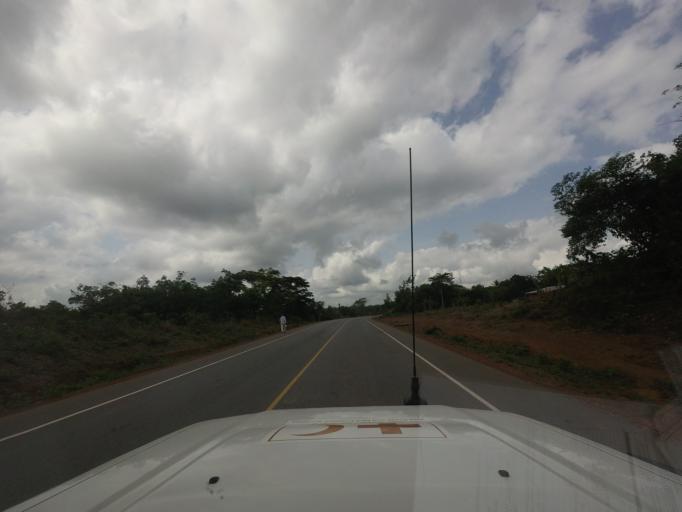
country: LR
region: Nimba
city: Sanniquellie
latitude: 7.1873
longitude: -9.0240
